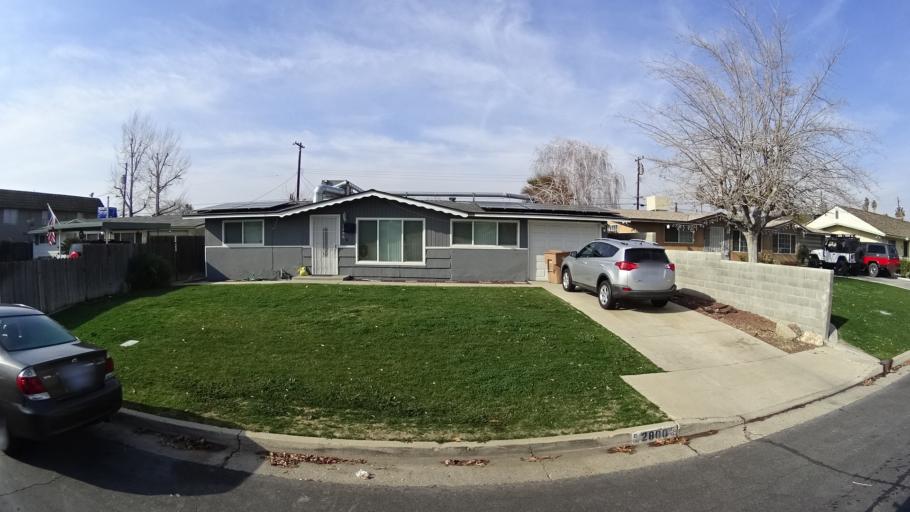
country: US
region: California
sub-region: Kern County
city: Oildale
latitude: 35.3987
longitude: -118.9753
